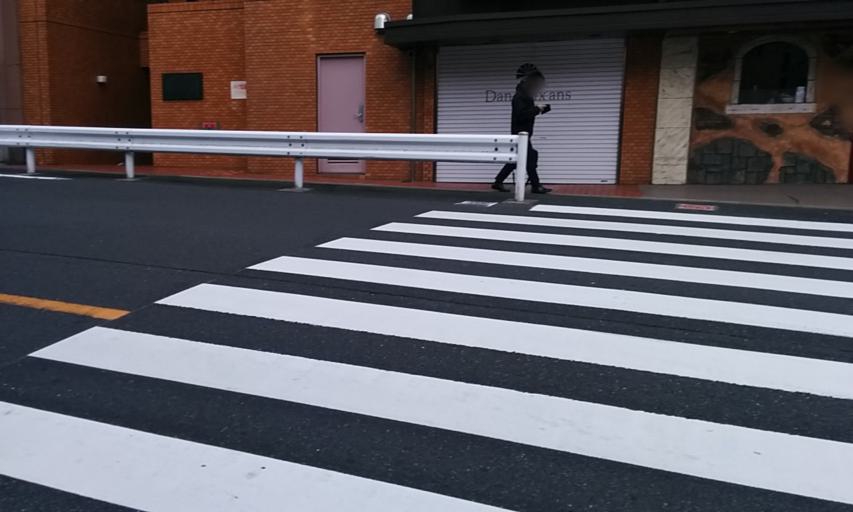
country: JP
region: Tokyo
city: Tokyo
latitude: 35.7044
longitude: 139.7308
